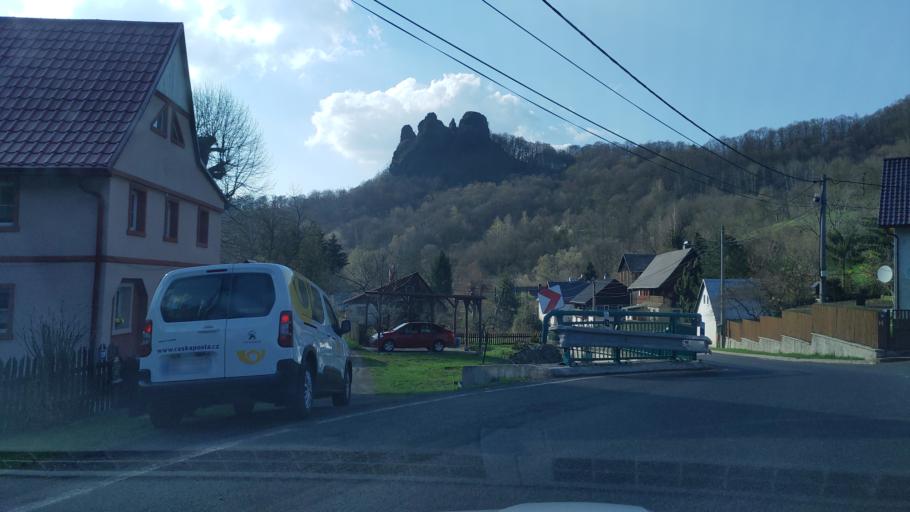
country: CZ
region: Ustecky
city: Povrly
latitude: 50.7069
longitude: 14.2193
